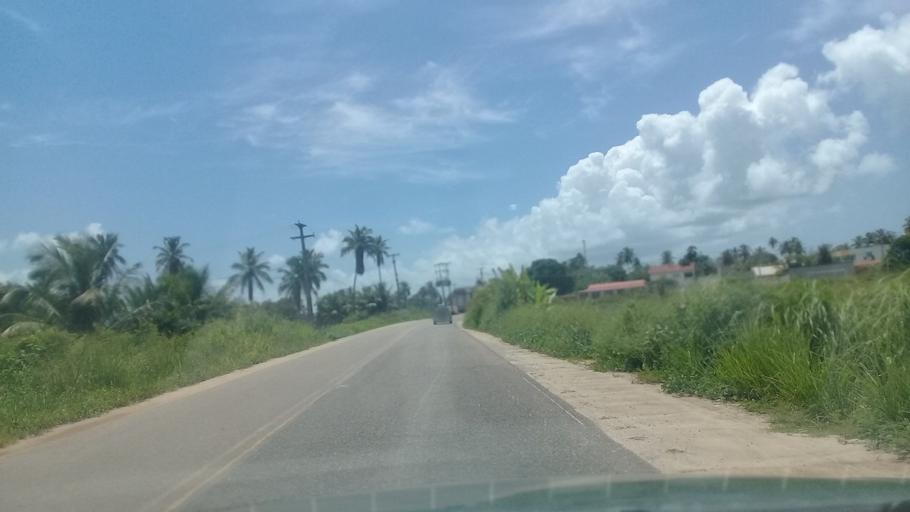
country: BR
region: Pernambuco
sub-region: Sirinhaem
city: Sirinhaem
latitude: -8.6249
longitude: -35.0646
